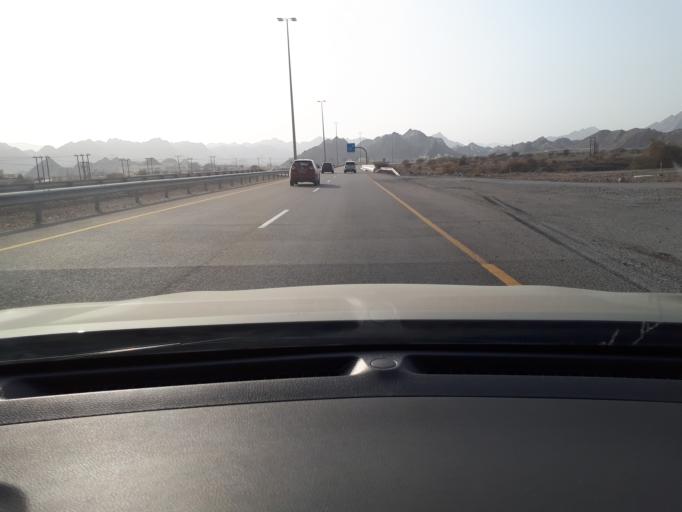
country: OM
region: Muhafazat Masqat
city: Muscat
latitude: 23.3030
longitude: 58.7352
